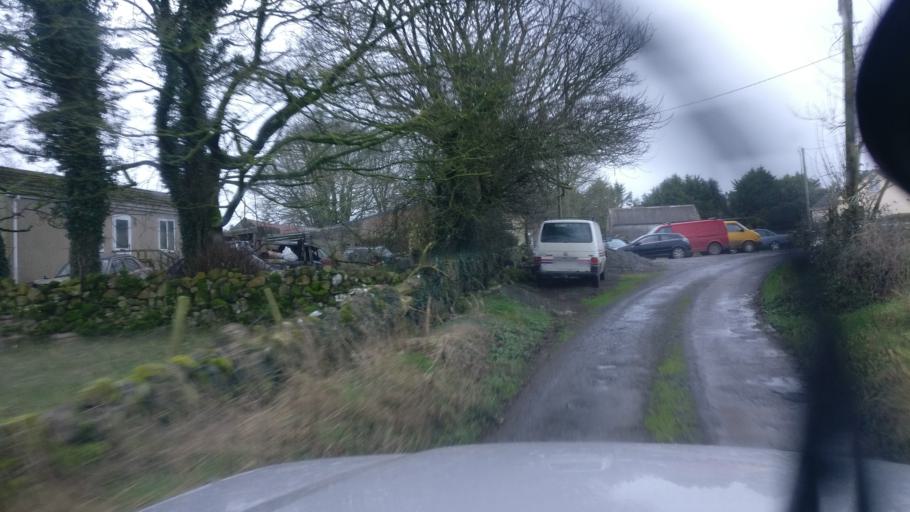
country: IE
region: Connaught
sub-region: County Galway
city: Loughrea
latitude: 53.2207
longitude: -8.5880
